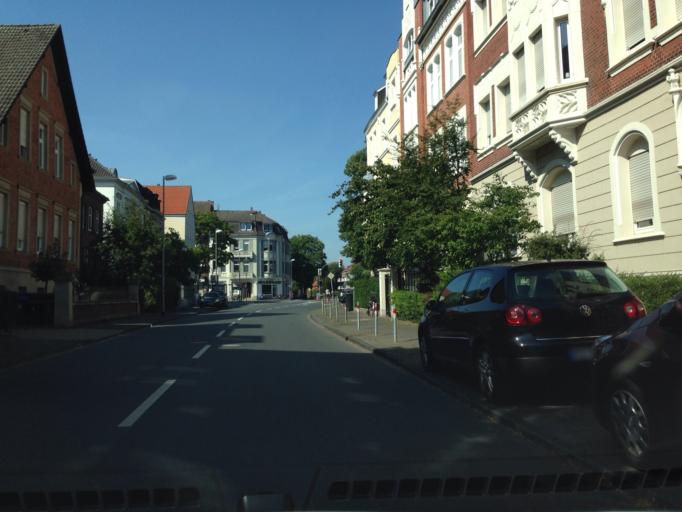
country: DE
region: North Rhine-Westphalia
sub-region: Regierungsbezirk Munster
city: Muenster
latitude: 51.9713
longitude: 7.6222
